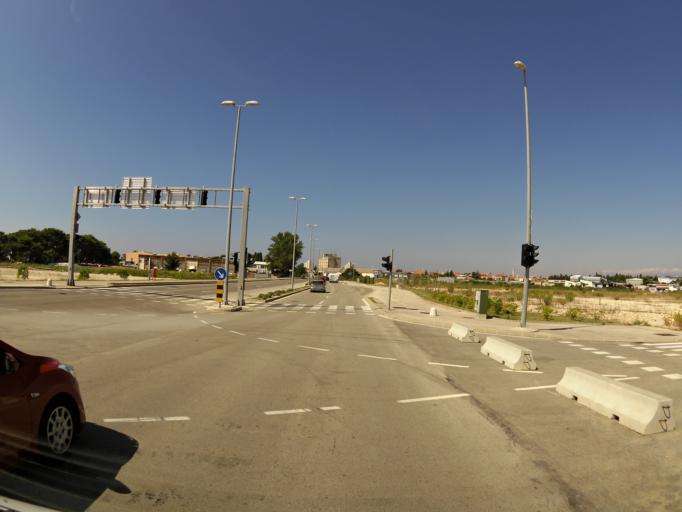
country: HR
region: Zadarska
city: Zadar
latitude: 44.0966
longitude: 15.2582
